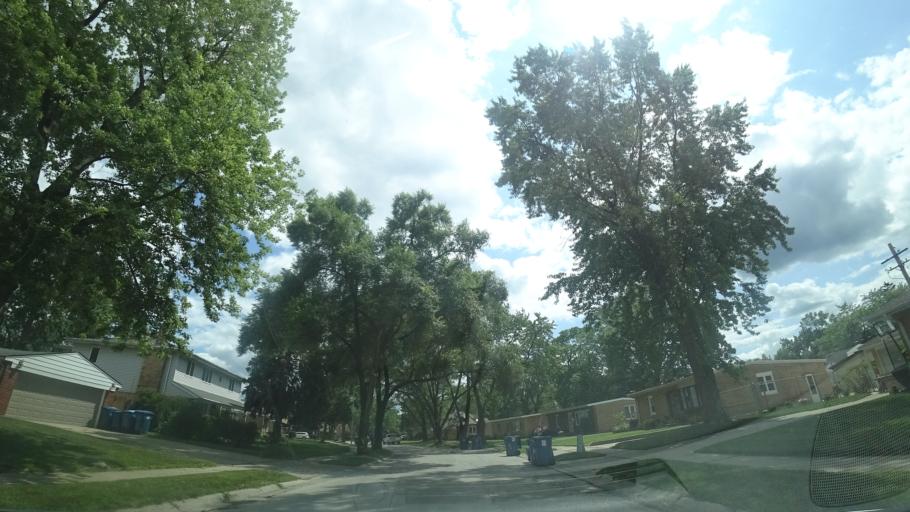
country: US
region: Illinois
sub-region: Cook County
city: Alsip
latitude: 41.6830
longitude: -87.7359
